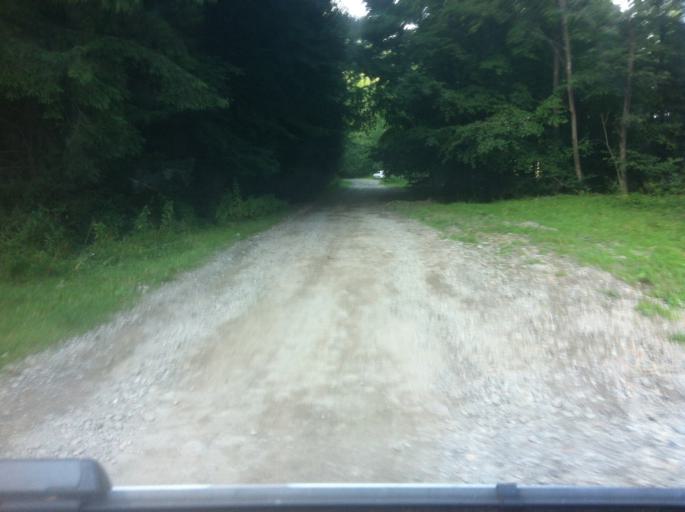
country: RO
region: Hunedoara
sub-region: Comuna Rau de Mori
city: Rau de Mori
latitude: 45.4365
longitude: 22.8930
